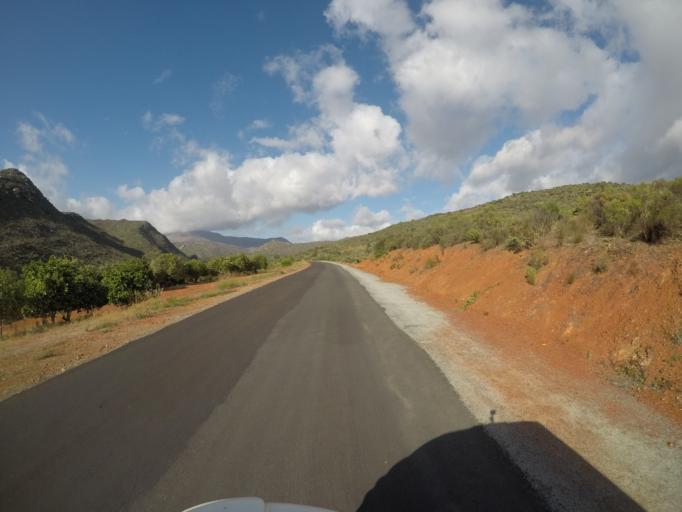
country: ZA
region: Western Cape
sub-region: West Coast District Municipality
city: Clanwilliam
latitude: -32.4339
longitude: 18.9472
